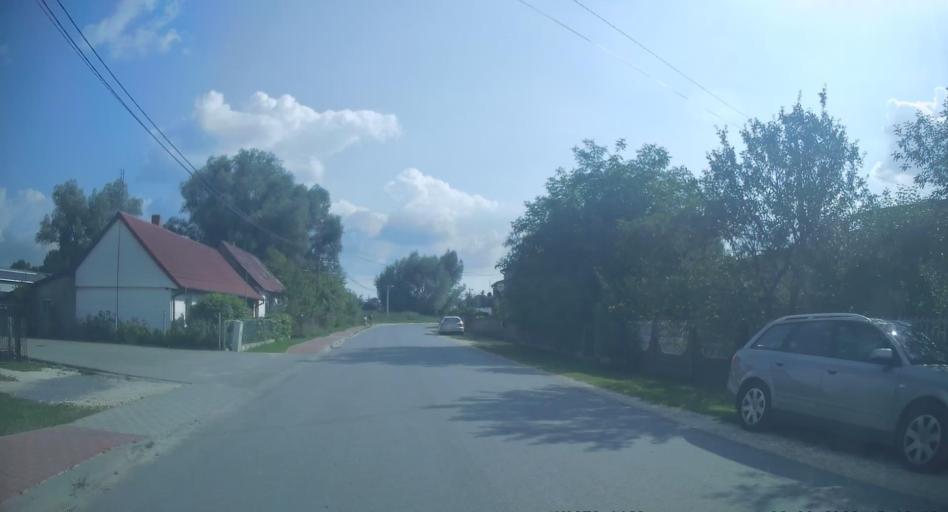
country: PL
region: Swietokrzyskie
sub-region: Powiat konecki
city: Radoszyce
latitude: 51.0808
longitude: 20.2576
